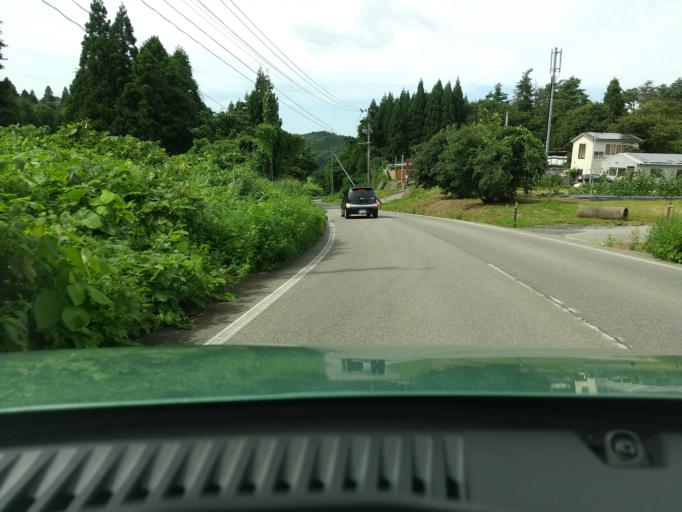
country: JP
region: Akita
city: Akita
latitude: 39.7769
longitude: 140.1346
